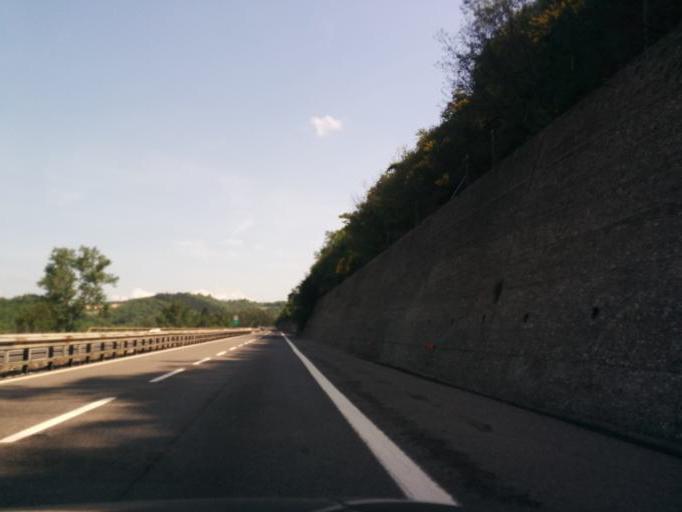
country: IT
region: Tuscany
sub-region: Province of Florence
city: Carraia
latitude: 43.9278
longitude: 11.2185
